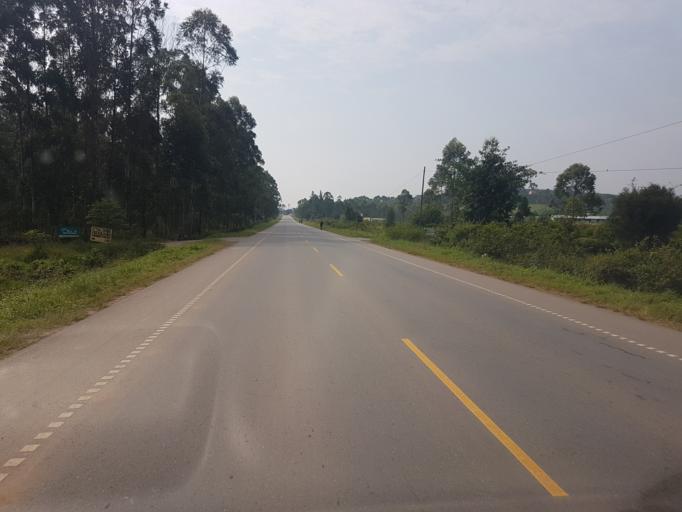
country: UG
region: Western Region
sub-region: Mbarara District
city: Bwizibwera
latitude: -0.6404
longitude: 30.5535
